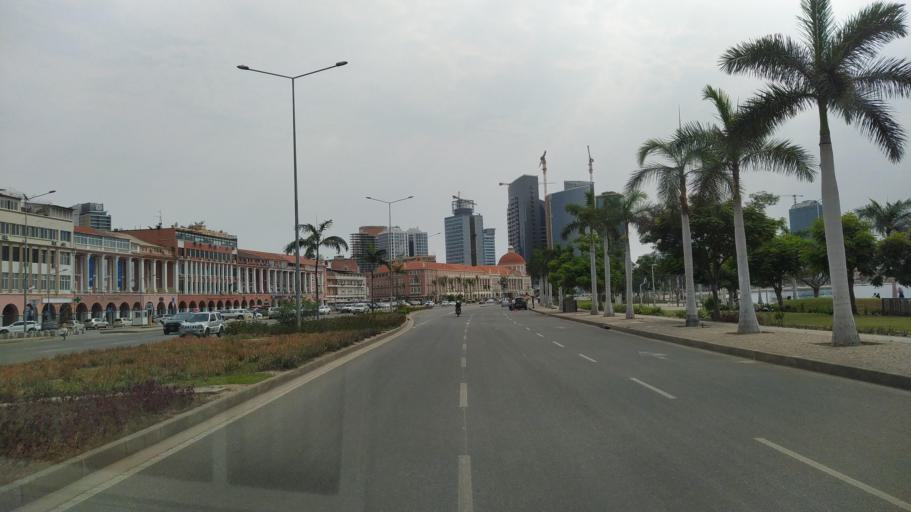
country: AO
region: Luanda
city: Luanda
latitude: -8.8082
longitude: 13.2374
